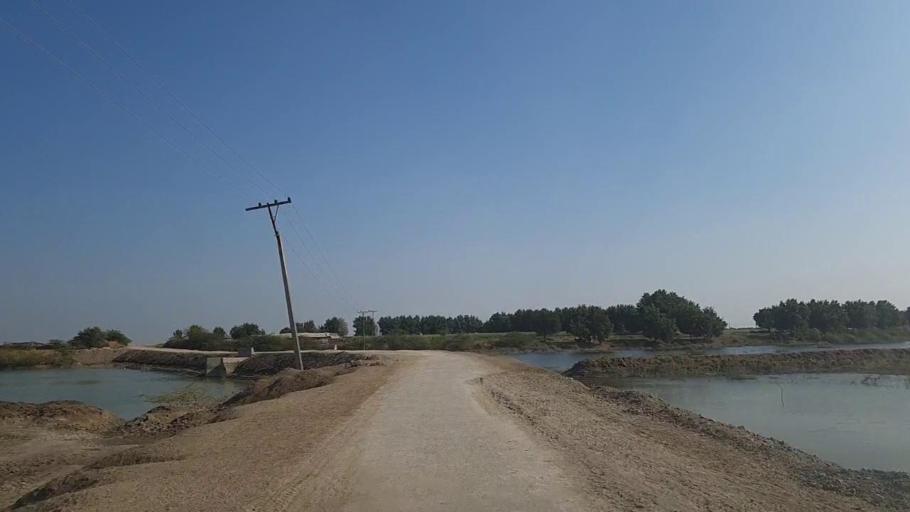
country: PK
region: Sindh
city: Digri
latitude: 25.0763
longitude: 69.2198
